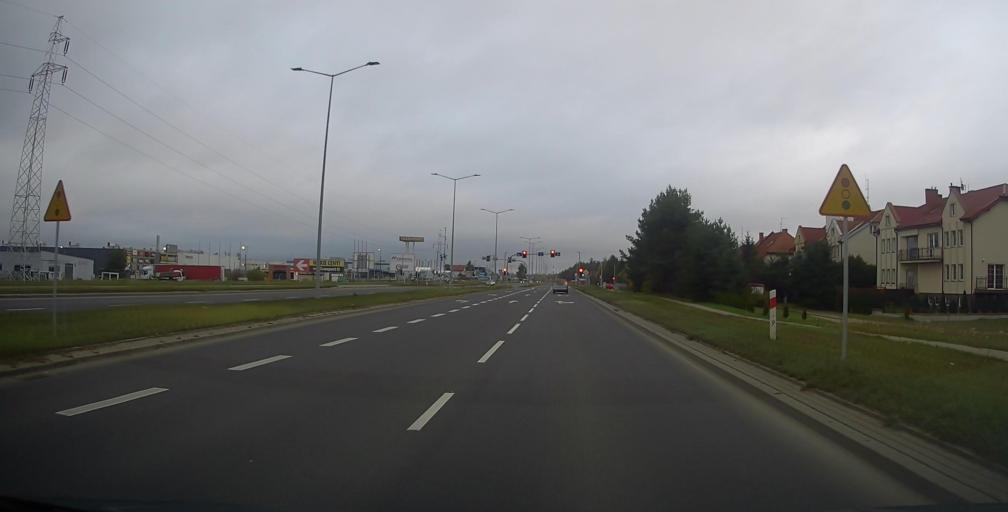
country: PL
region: Warmian-Masurian Voivodeship
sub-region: Powiat elcki
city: Elk
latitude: 53.8103
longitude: 22.3774
